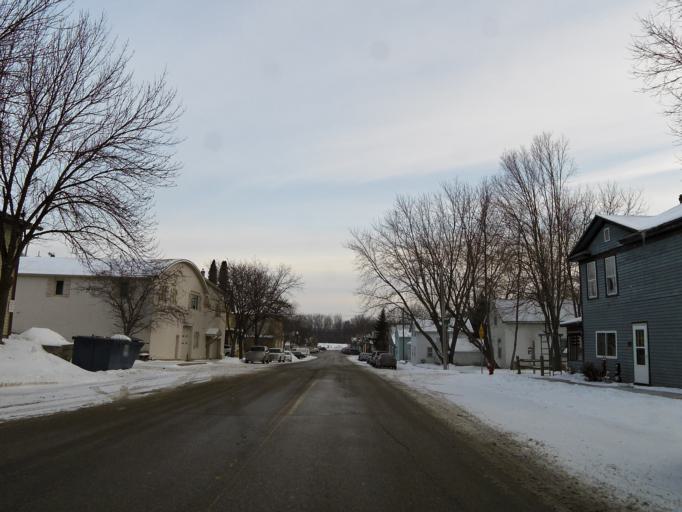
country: US
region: Minnesota
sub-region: Carver County
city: Carver
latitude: 44.7645
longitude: -93.6269
